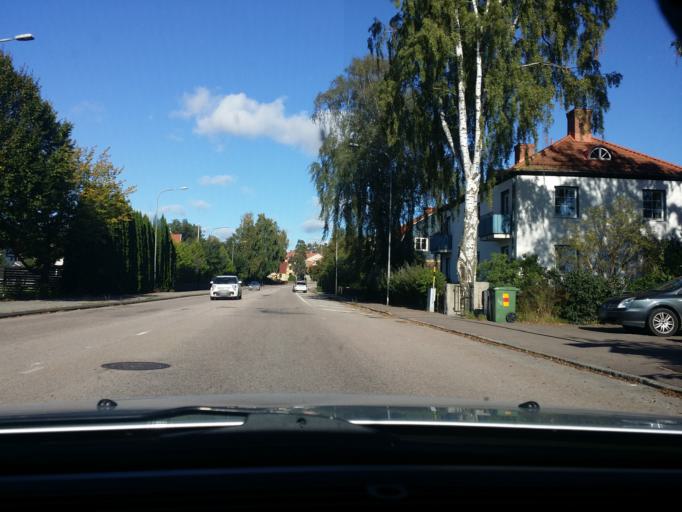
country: SE
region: Vaestmanland
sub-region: Vasteras
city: Vasteras
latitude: 59.6222
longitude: 16.5750
